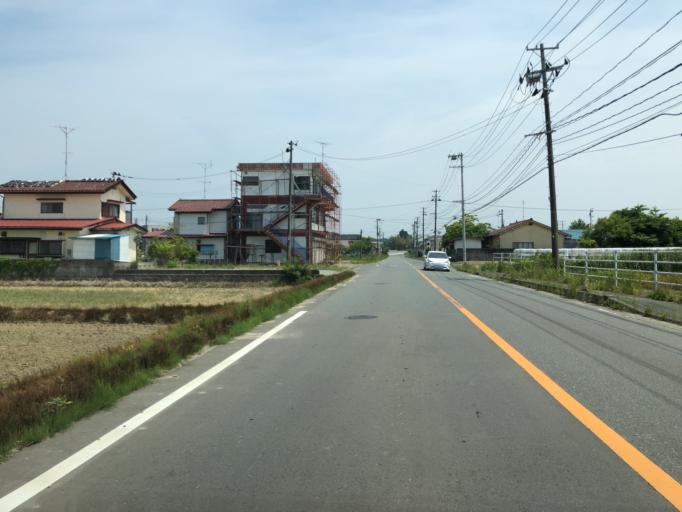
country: JP
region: Fukushima
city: Namie
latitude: 37.4884
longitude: 140.9946
